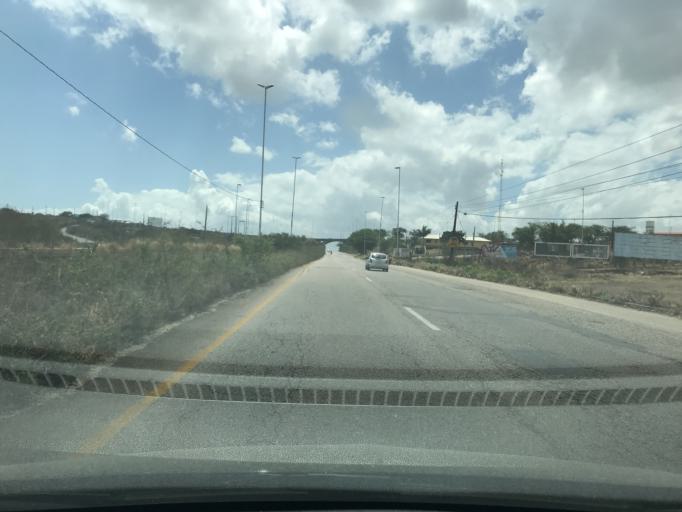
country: BR
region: Pernambuco
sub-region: Caruaru
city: Caruaru
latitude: -8.3067
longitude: -35.9611
